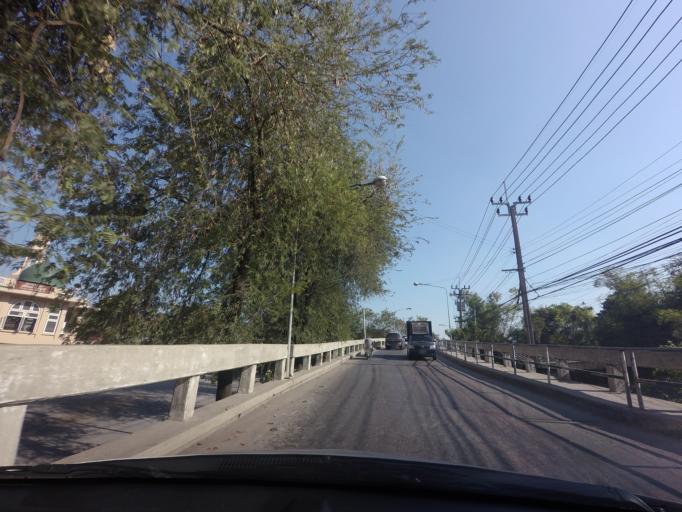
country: TH
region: Bangkok
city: Nong Chok
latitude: 13.8583
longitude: 100.8541
